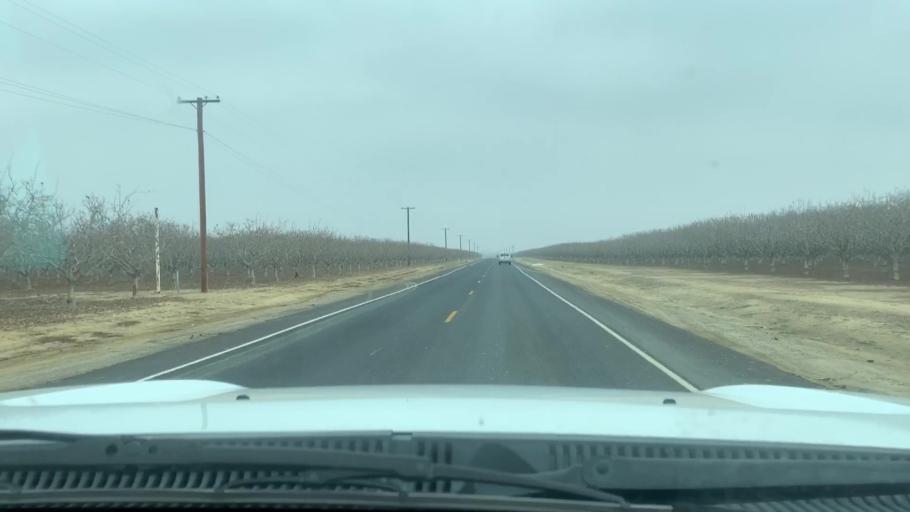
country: US
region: California
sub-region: Kern County
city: Lost Hills
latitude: 35.4993
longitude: -119.6435
